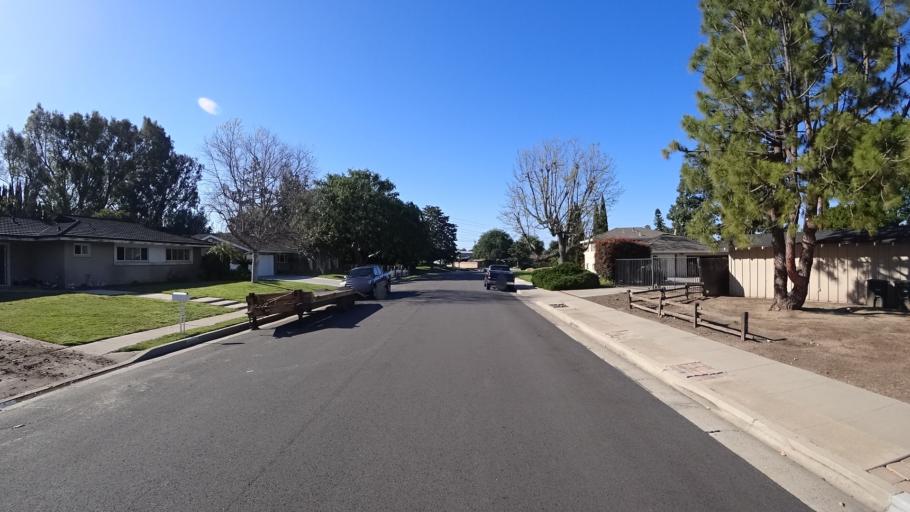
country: US
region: California
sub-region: Orange County
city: Villa Park
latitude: 33.8256
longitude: -117.8250
